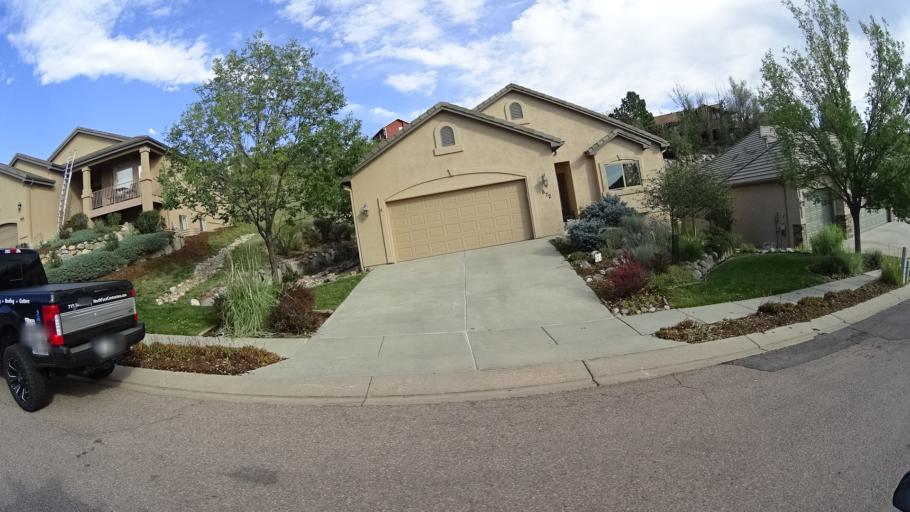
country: US
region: Colorado
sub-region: El Paso County
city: Stratmoor
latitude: 38.7667
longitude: -104.8191
